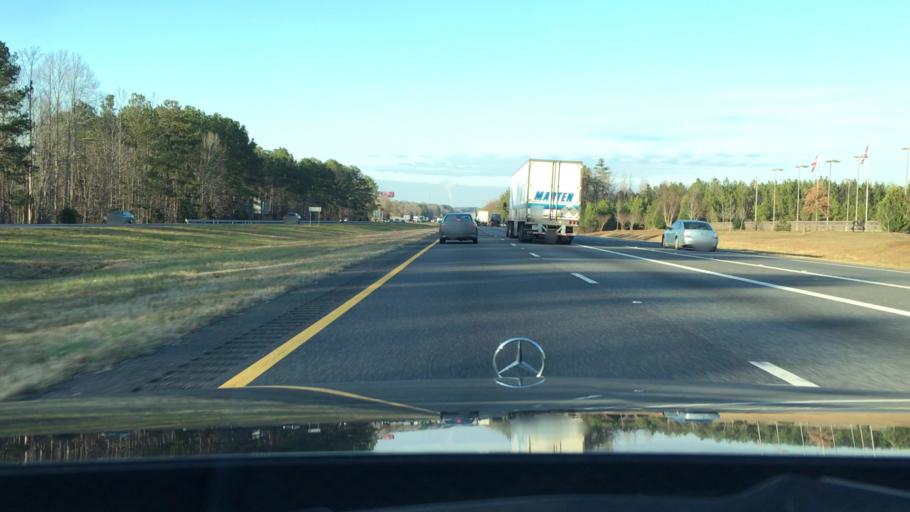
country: US
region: South Carolina
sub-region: Chester County
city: Eureka Mill
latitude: 34.7493
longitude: -81.0357
